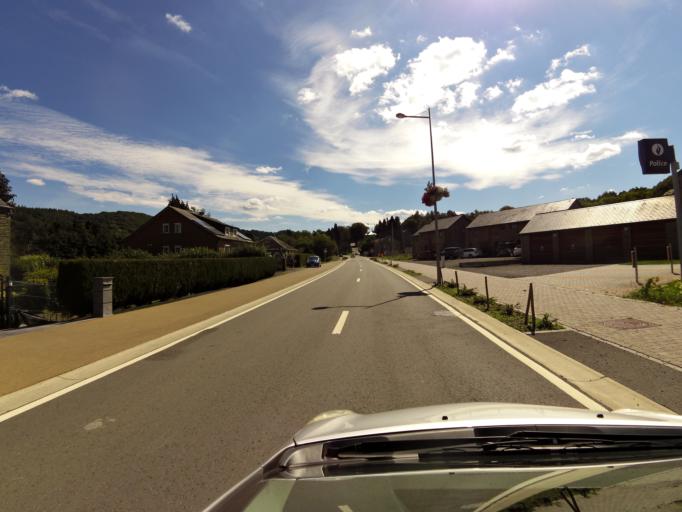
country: BE
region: Wallonia
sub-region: Province du Luxembourg
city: Rendeux
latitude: 50.2320
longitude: 5.5138
